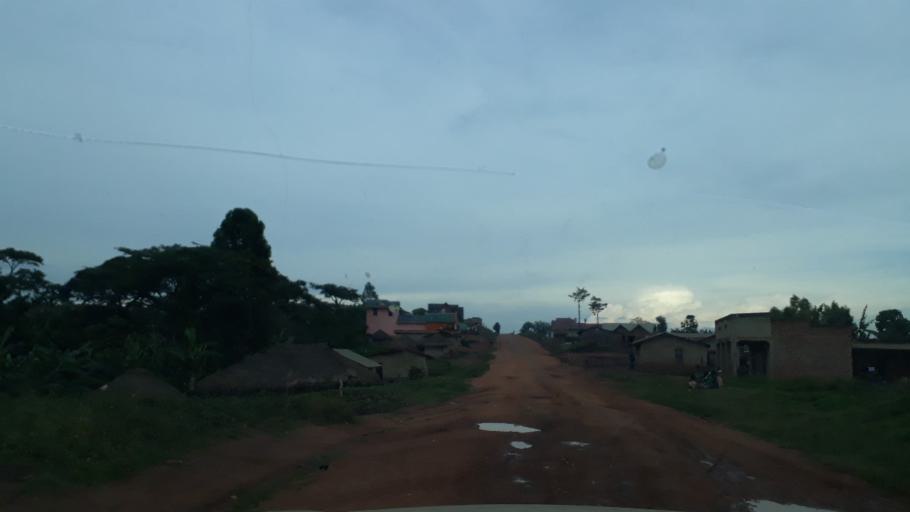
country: UG
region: Northern Region
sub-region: Zombo District
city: Paidha
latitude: 2.2013
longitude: 30.7280
